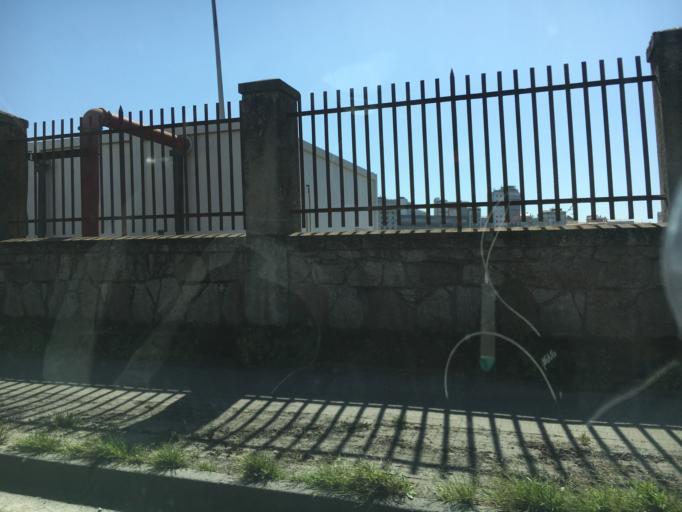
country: ES
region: Galicia
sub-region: Provincia da Coruna
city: A Coruna
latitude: 43.3576
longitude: -8.3958
